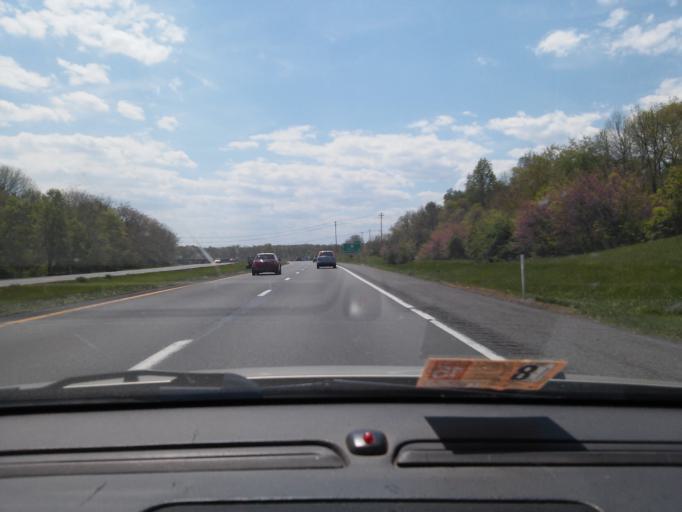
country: US
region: West Virginia
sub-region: Berkeley County
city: Inwood
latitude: 39.4114
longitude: -78.0186
